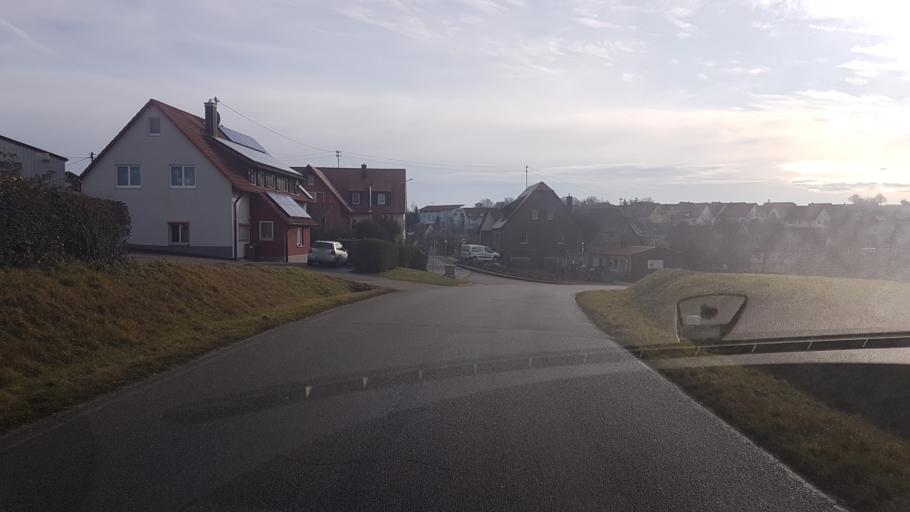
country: DE
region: Baden-Wuerttemberg
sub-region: Regierungsbezirk Stuttgart
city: Braunsbach
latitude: 49.2054
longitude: 9.7380
